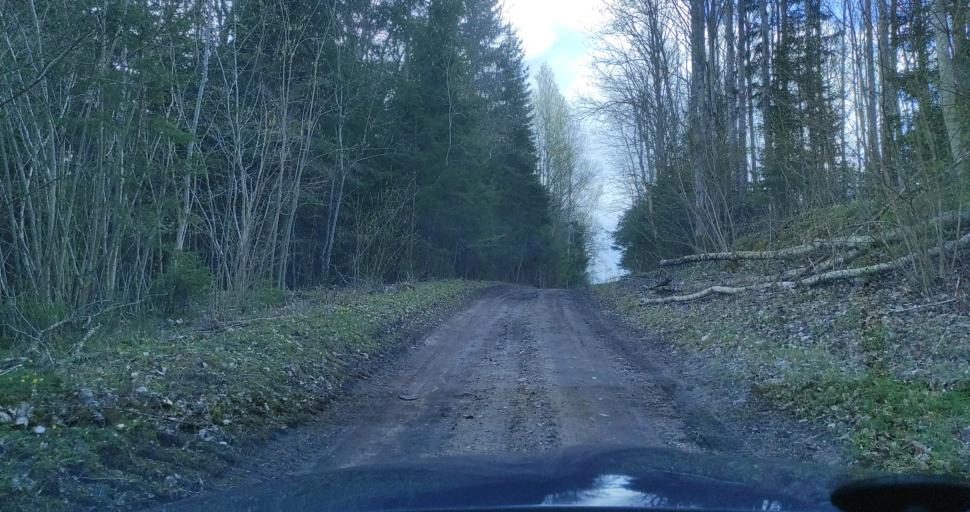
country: LV
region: Kuldigas Rajons
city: Kuldiga
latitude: 56.8630
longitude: 21.8303
